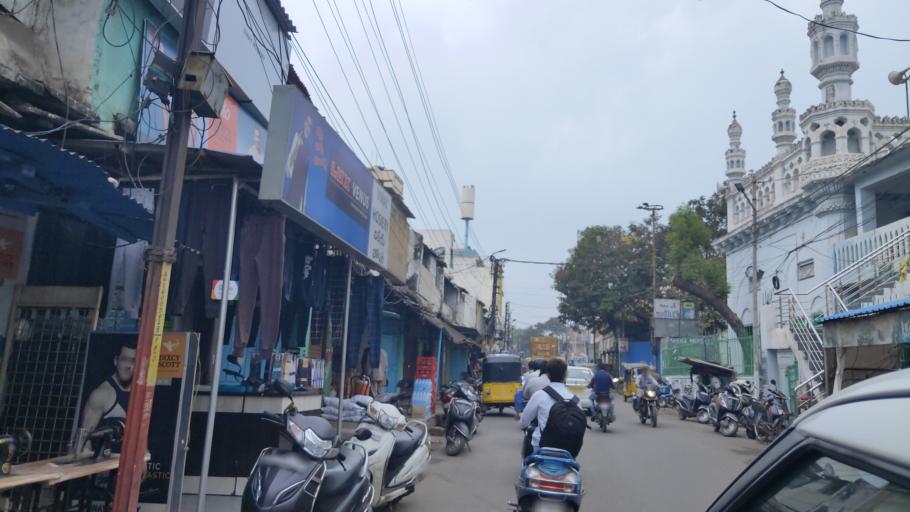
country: IN
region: Telangana
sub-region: Hyderabad
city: Hyderabad
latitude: 17.3681
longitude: 78.4849
